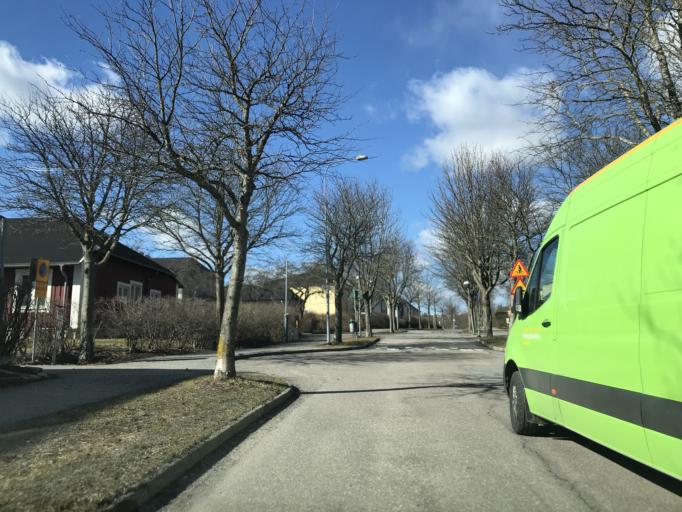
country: SE
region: Stockholm
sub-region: Stockholms Kommun
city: Kista
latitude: 59.3969
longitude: 17.9391
